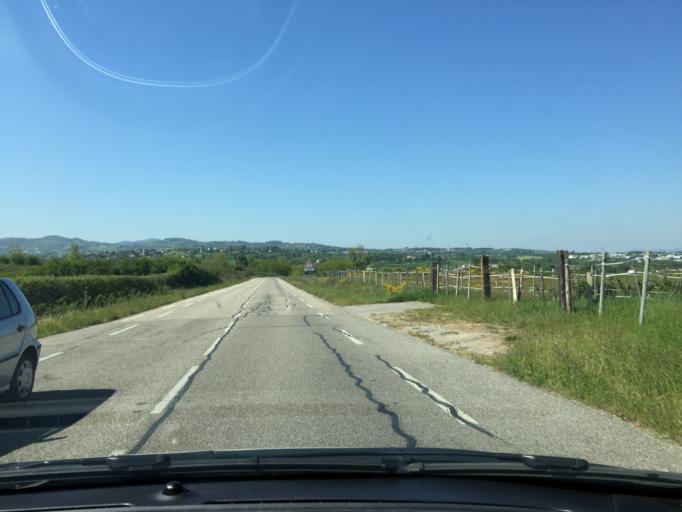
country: FR
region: Rhone-Alpes
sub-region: Departement du Rhone
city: Saint-Andeol-le-Chateau
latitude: 45.5962
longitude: 4.6953
